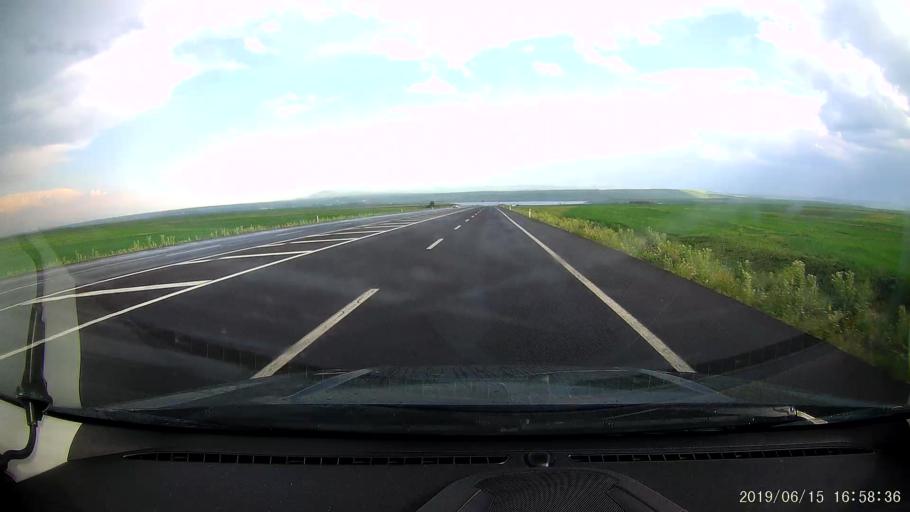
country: TR
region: Kars
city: Susuz
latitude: 40.7631
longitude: 43.1442
